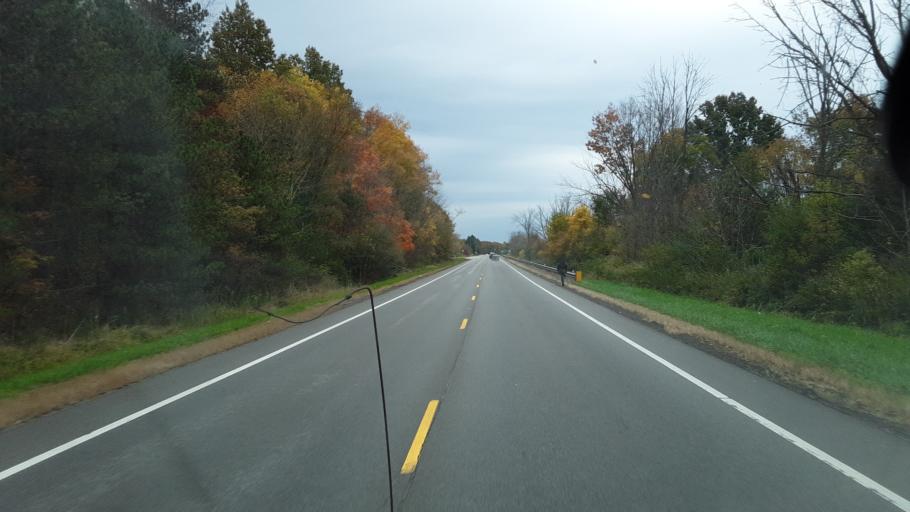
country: US
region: Ohio
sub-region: Portage County
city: Ravenna
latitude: 41.1794
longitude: -81.2548
